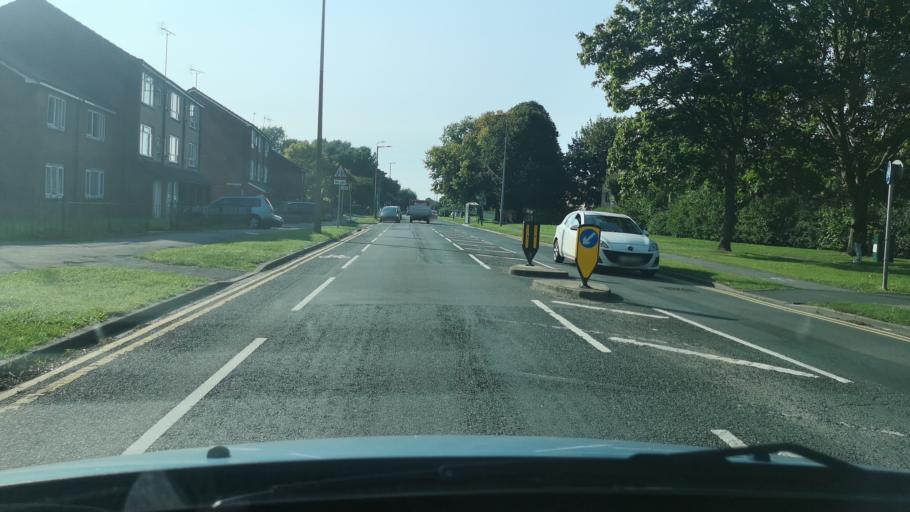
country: GB
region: England
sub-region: North Lincolnshire
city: Scunthorpe
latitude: 53.5742
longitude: -0.6793
